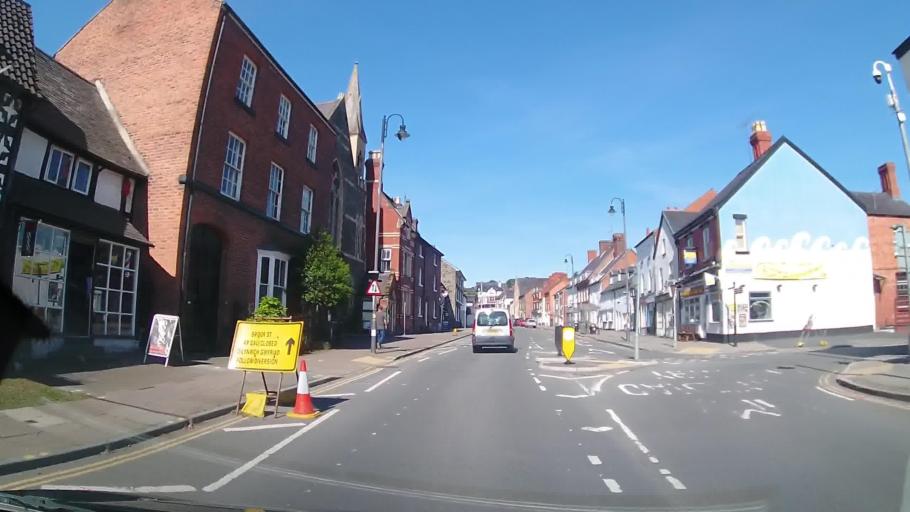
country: GB
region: Wales
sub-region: Sir Powys
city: Welshpool
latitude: 52.6607
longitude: -3.1500
